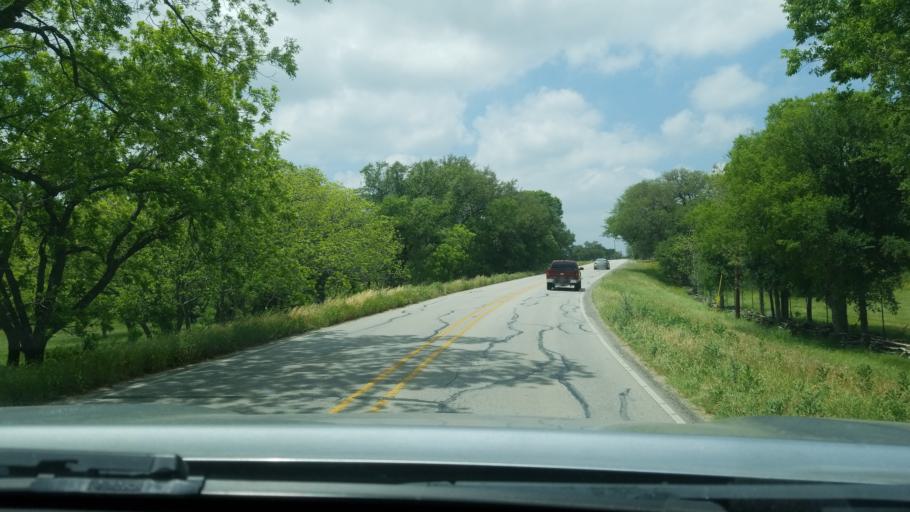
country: US
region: Texas
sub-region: Hays County
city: Dripping Springs
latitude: 30.1316
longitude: -98.0179
